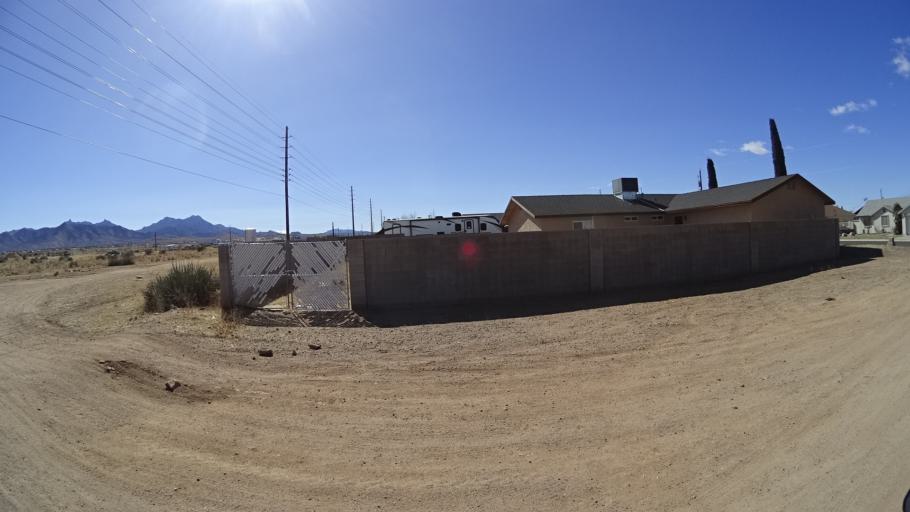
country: US
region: Arizona
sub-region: Mohave County
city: New Kingman-Butler
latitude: 35.2194
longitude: -113.9939
